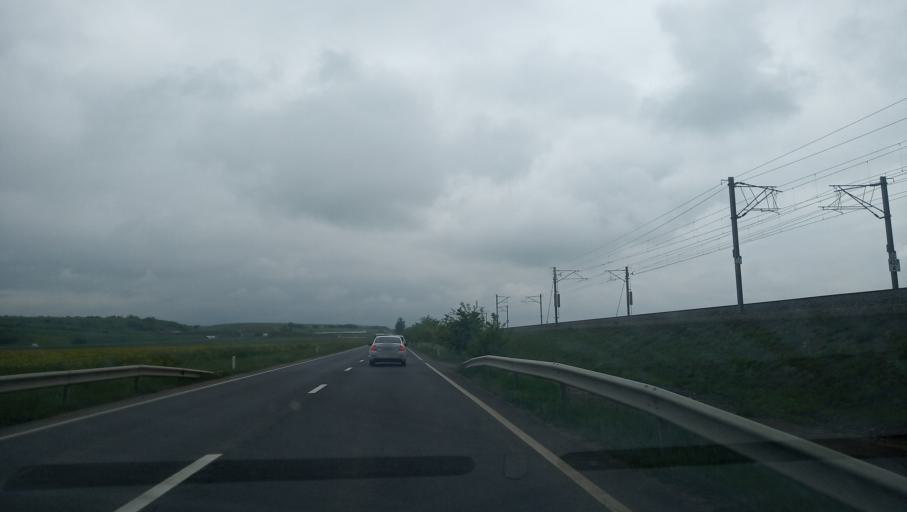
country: RO
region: Alba
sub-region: Comuna Saliste
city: Salistea
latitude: 45.9372
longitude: 23.3782
